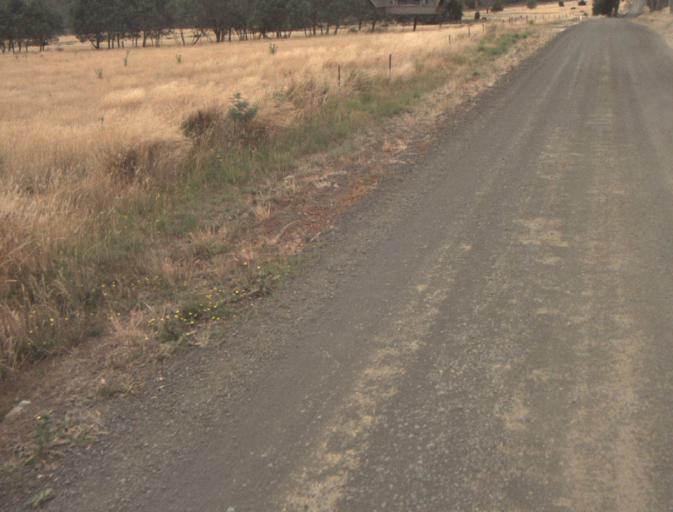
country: AU
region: Tasmania
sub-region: Northern Midlands
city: Evandale
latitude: -41.5253
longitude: 147.3628
